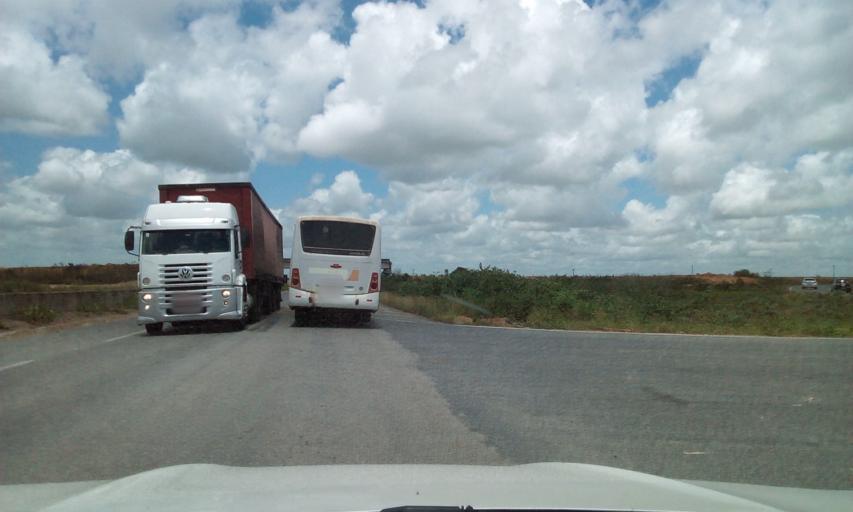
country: BR
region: Alagoas
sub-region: Sao Miguel Dos Campos
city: Sao Miguel dos Campos
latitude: -9.7578
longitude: -36.0696
